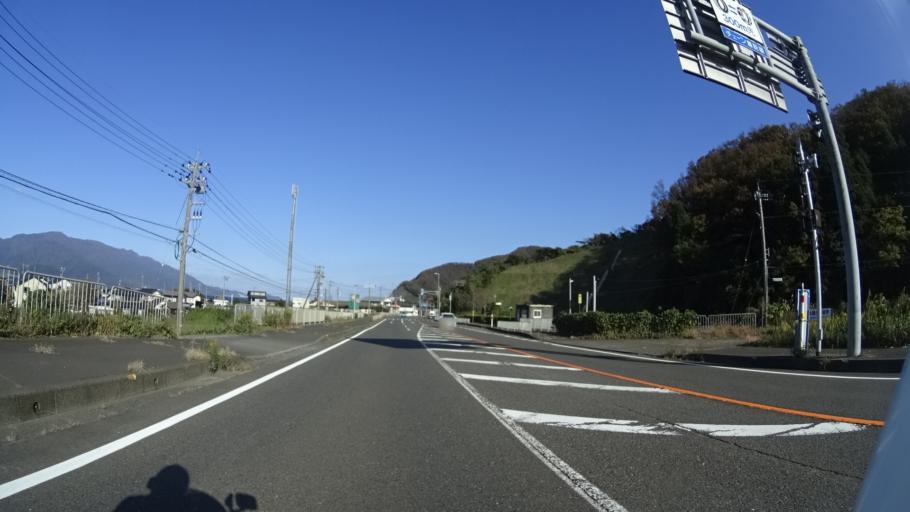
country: JP
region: Fukui
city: Tsuruga
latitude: 35.6788
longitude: 136.0860
